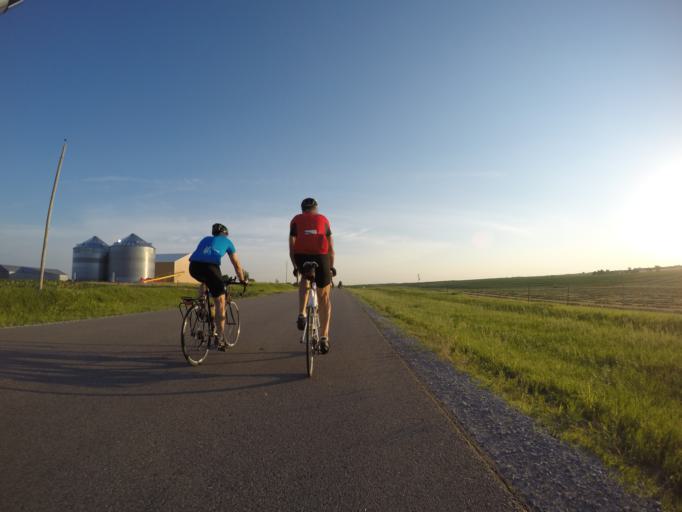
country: US
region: Kansas
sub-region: Marshall County
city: Marysville
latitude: 39.8546
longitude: -96.6009
